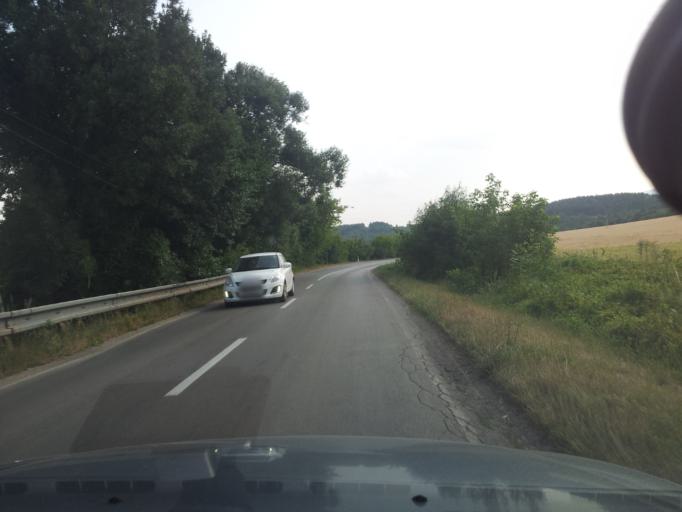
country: SK
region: Nitriansky
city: Trencianske Teplice
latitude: 48.8264
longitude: 18.1823
